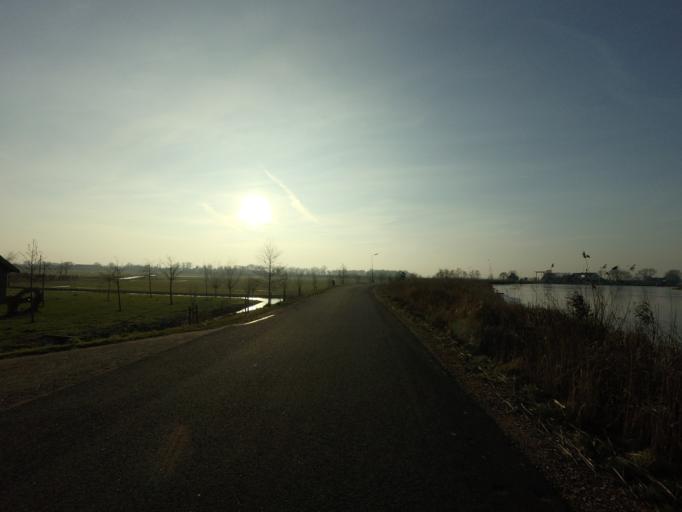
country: NL
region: North Holland
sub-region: Gemeente Ouder-Amstel
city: Ouderkerk aan de Amstel
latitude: 52.2794
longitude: 4.9293
